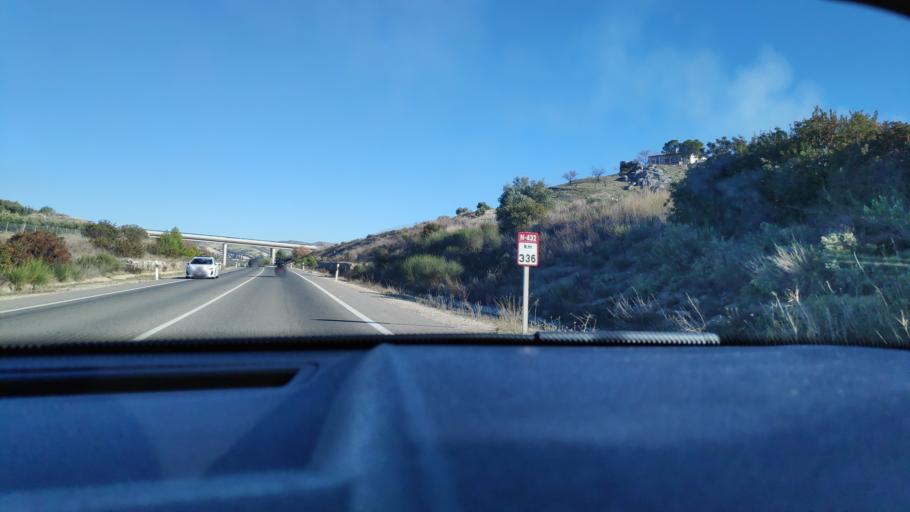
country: ES
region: Andalusia
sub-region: Province of Cordoba
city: Baena
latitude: 37.6060
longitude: -4.3027
